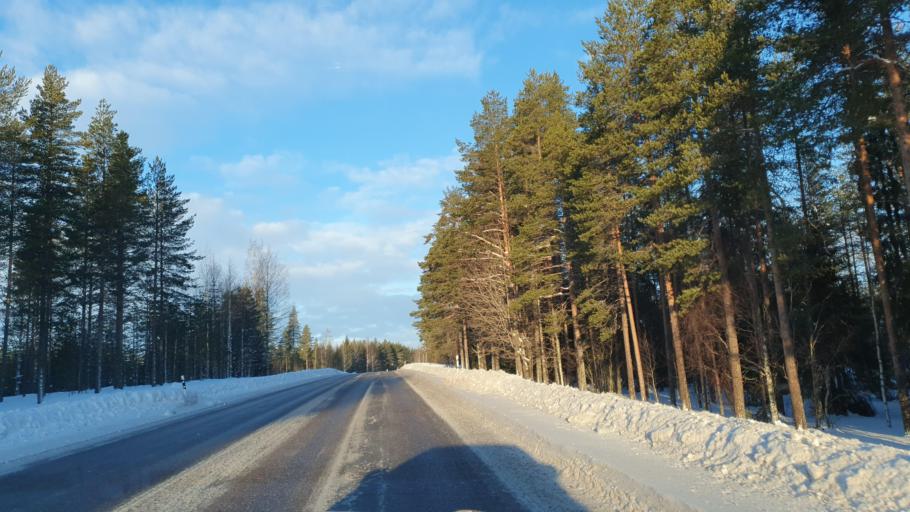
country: FI
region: Kainuu
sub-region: Kajaani
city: Vuolijoki
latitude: 64.4868
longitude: 27.3308
